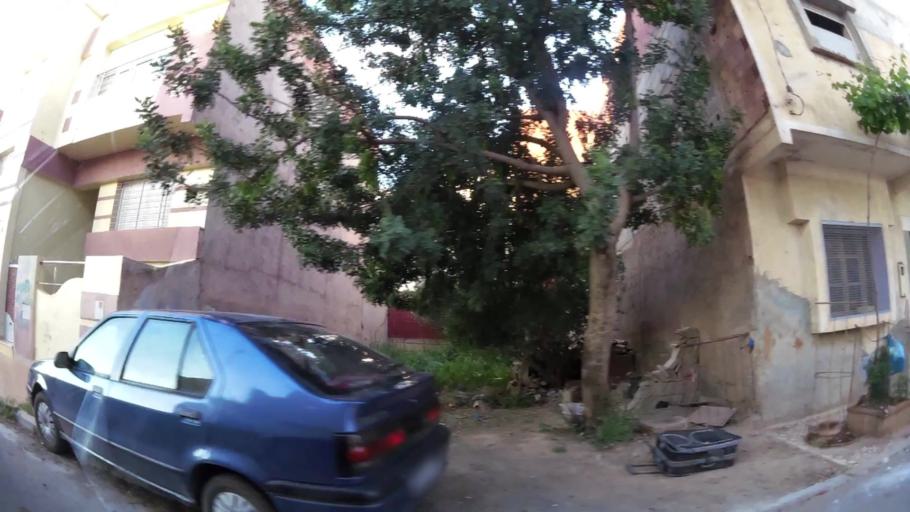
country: MA
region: Oriental
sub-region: Oujda-Angad
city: Oujda
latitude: 34.7120
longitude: -1.9217
